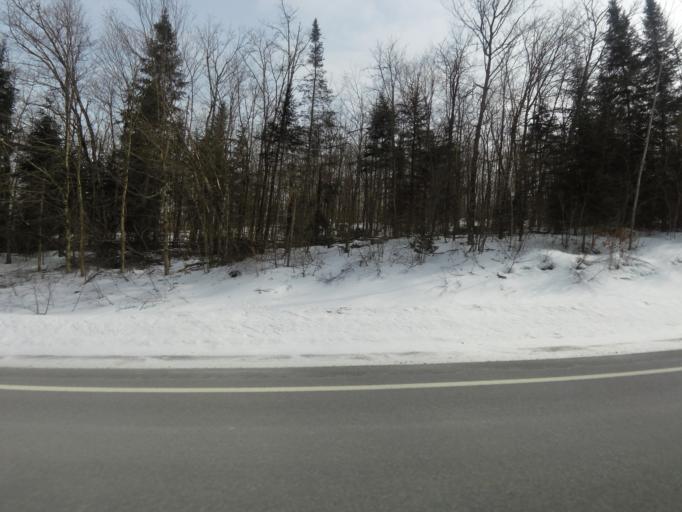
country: CA
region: Quebec
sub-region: Laurentides
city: Ferme-Neuve
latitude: 46.7176
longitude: -75.3143
